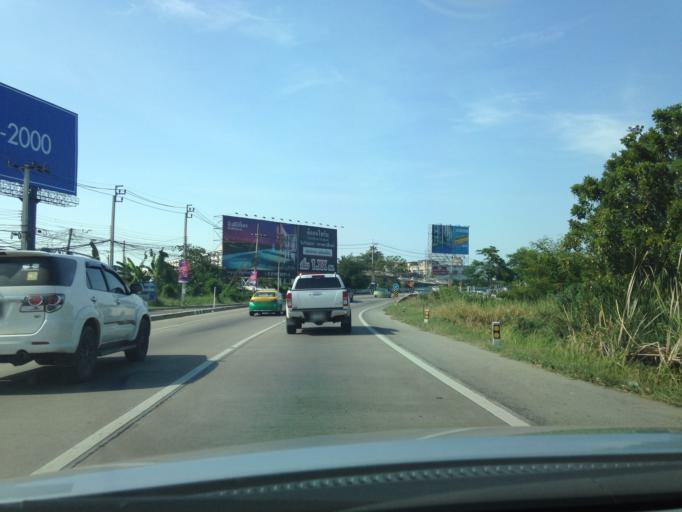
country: TH
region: Nonthaburi
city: Bang Bua Thong
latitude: 13.8716
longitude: 100.4089
